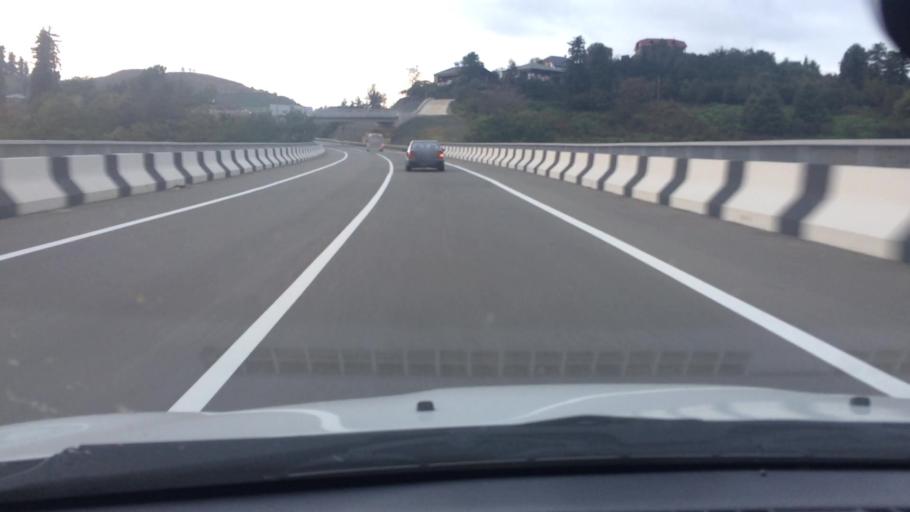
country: GE
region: Ajaria
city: Makhinjauri
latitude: 41.7168
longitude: 41.7518
